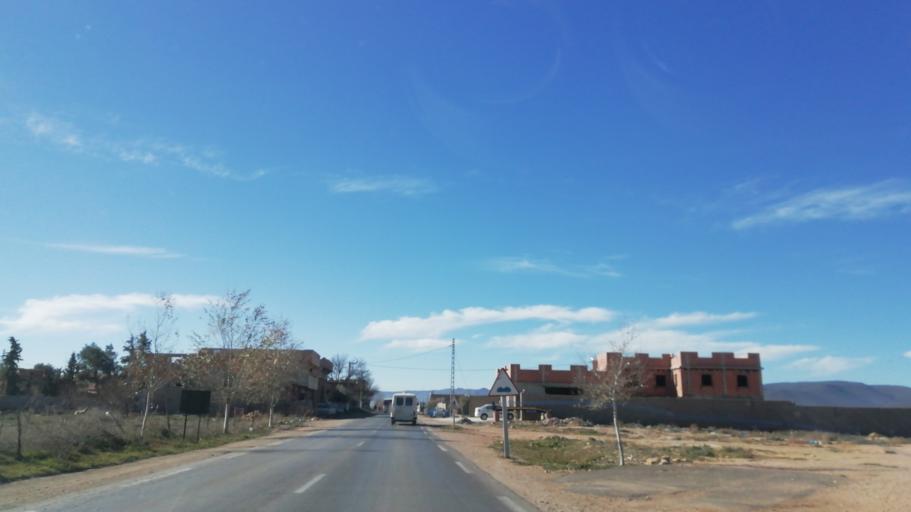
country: DZ
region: Tlemcen
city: Sebdou
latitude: 34.6655
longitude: -1.2871
